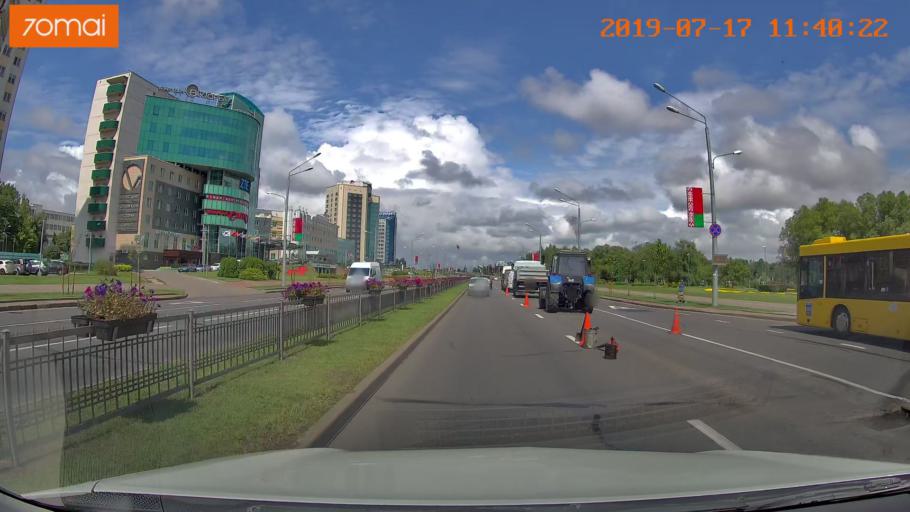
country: BY
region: Minsk
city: Minsk
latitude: 53.9208
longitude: 27.5295
